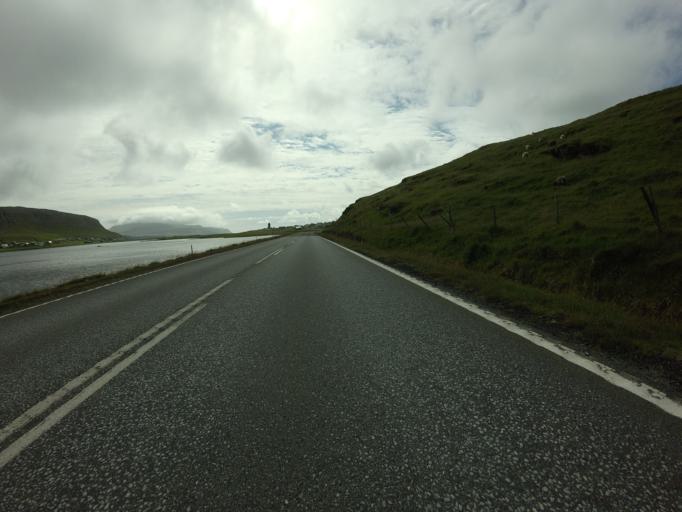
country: FO
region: Sandoy
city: Sandur
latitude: 61.8466
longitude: -6.8278
